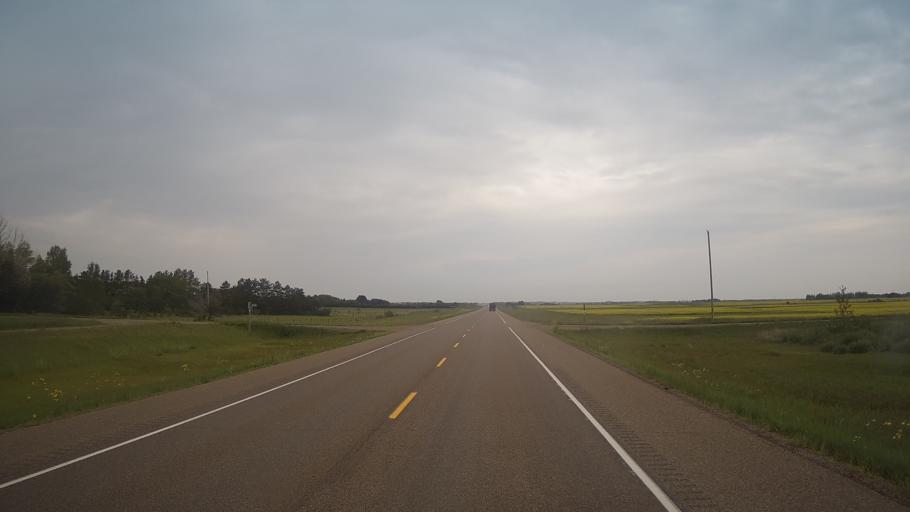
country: CA
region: Saskatchewan
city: Langham
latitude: 52.1294
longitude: -107.0734
